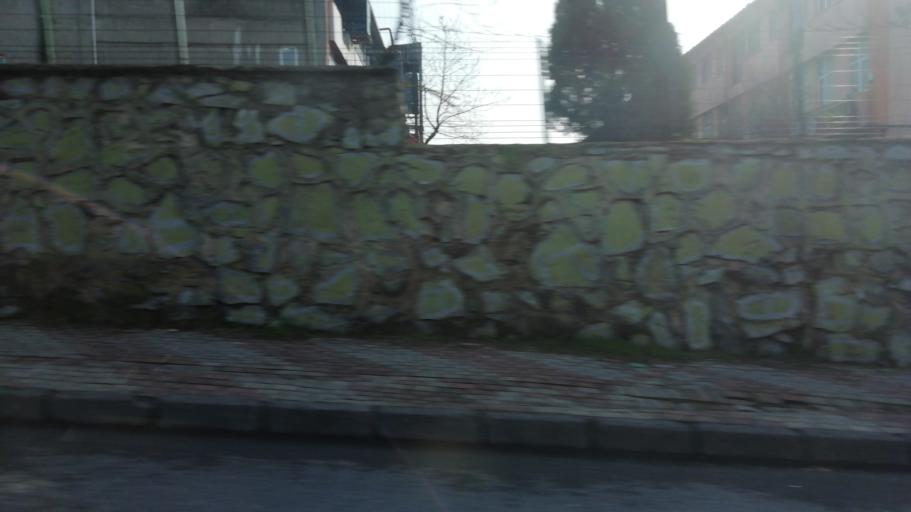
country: TR
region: Istanbul
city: Basaksehir
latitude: 41.0952
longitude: 28.7949
